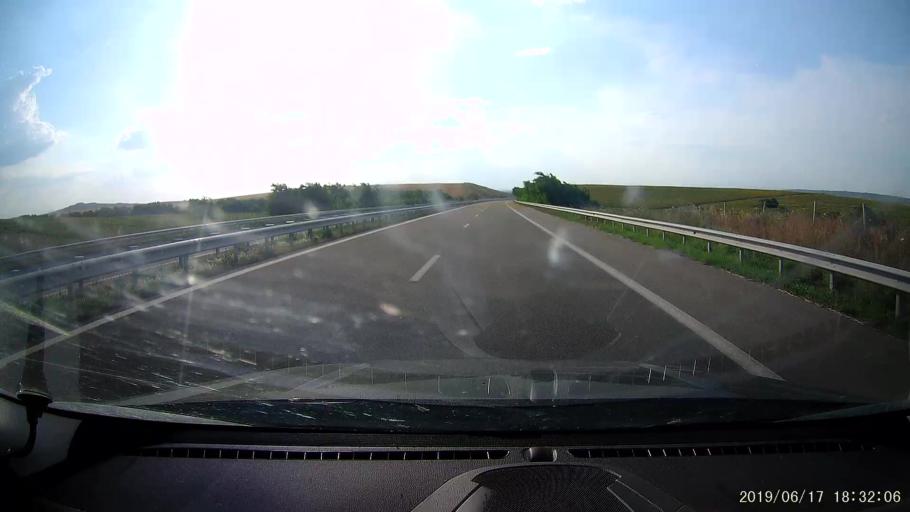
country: BG
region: Khaskovo
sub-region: Obshtina Dimitrovgrad
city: Dimitrovgrad
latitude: 42.0548
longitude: 25.4871
